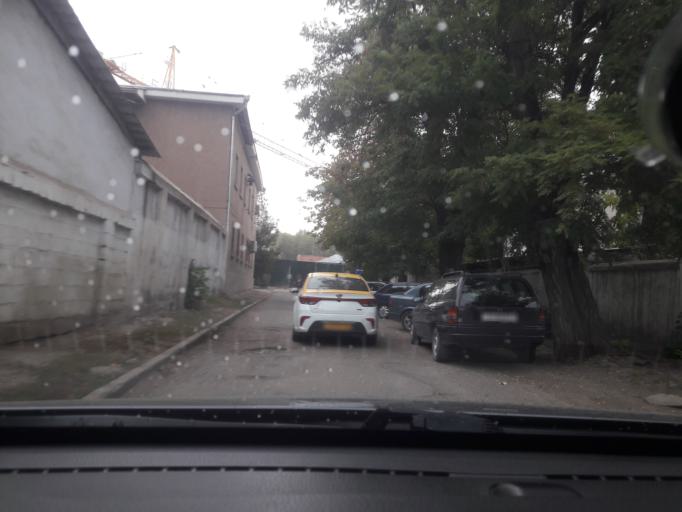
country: TJ
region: Dushanbe
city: Dushanbe
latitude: 38.5653
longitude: 68.7918
